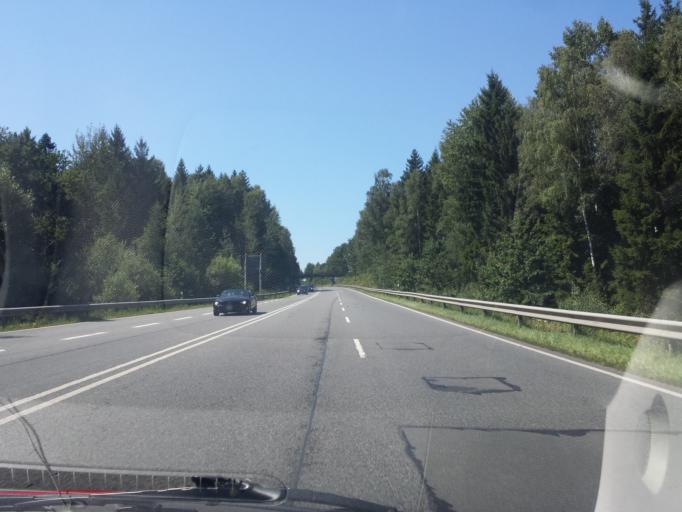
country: DE
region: Bavaria
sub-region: Upper Palatinate
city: Arnschwang
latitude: 49.2910
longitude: 12.8226
